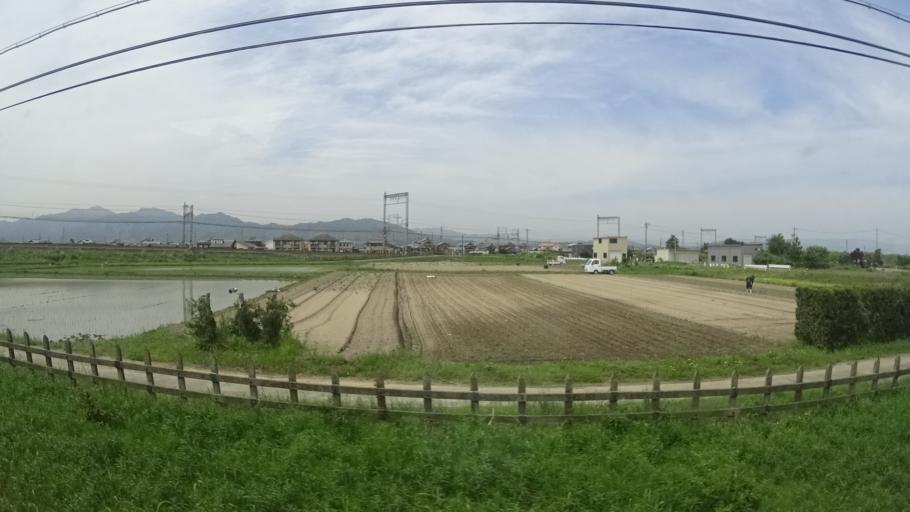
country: JP
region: Mie
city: Hisai-motomachi
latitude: 34.6074
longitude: 136.5083
